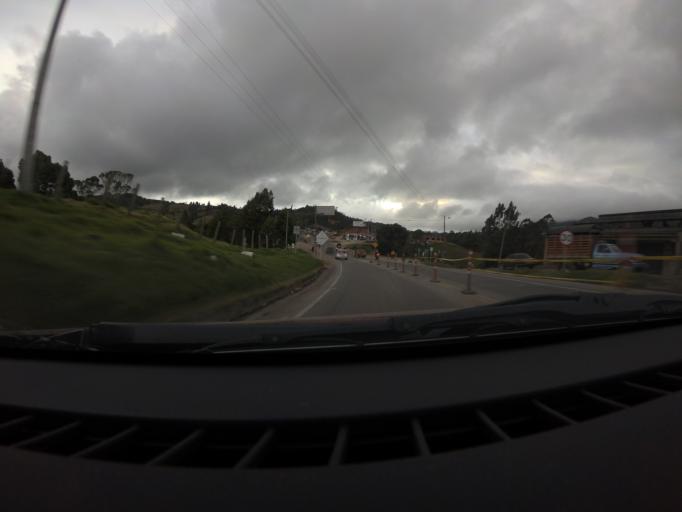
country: CO
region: Boyaca
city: Samaca
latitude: 5.4459
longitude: -73.4351
